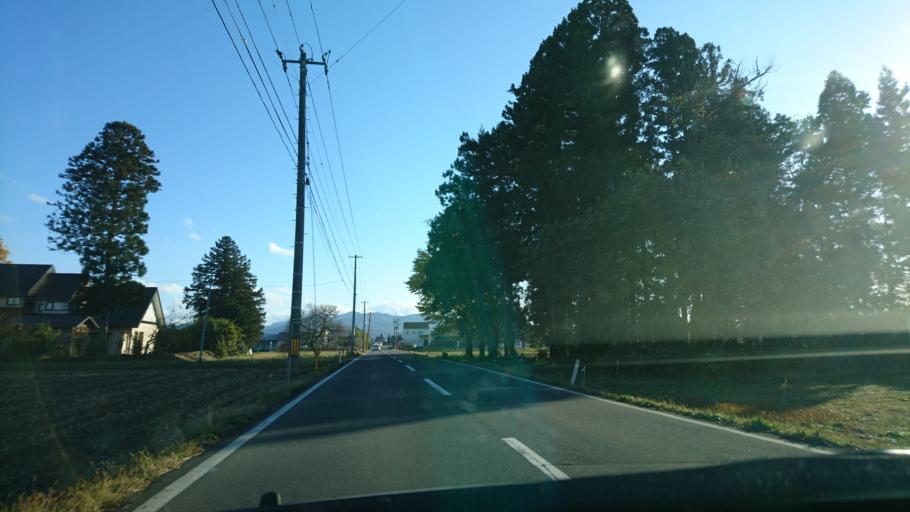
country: JP
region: Iwate
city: Mizusawa
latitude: 39.1033
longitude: 141.1571
